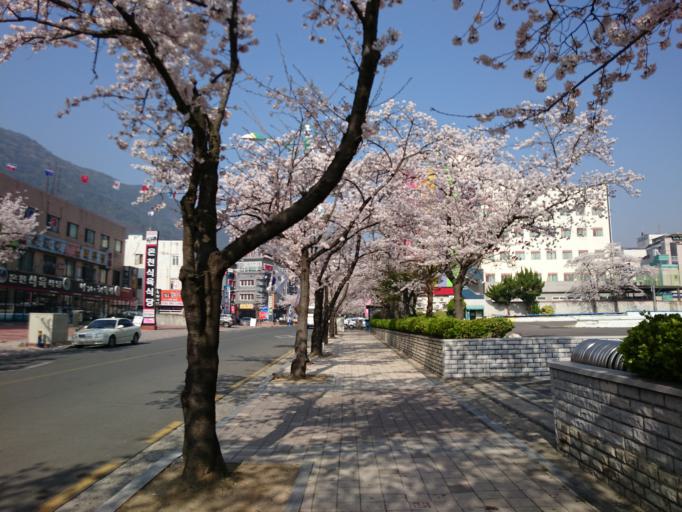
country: KR
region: Gyeongsangnam-do
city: Changnyeong
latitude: 35.4386
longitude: 128.5909
